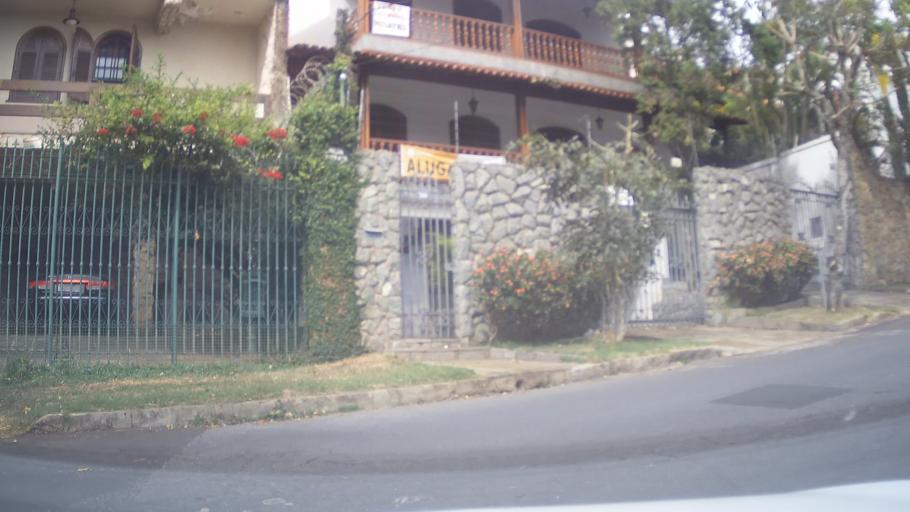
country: BR
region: Minas Gerais
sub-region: Belo Horizonte
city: Belo Horizonte
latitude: -19.9548
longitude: -43.9209
